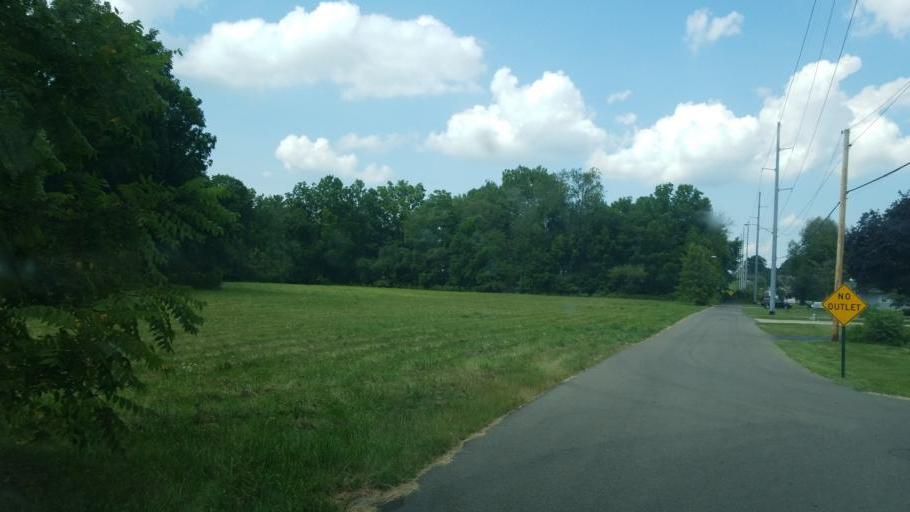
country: US
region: Ohio
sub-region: Knox County
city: Mount Vernon
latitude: 40.3950
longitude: -82.4672
